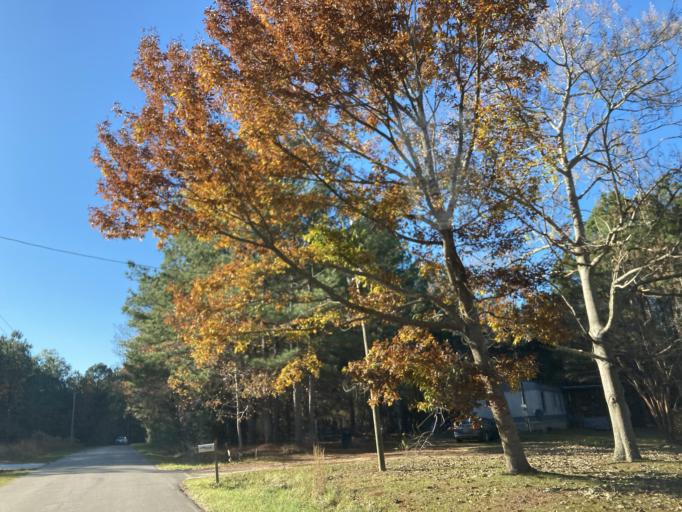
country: US
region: Mississippi
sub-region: Lamar County
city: Sumrall
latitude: 31.3656
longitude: -89.5620
